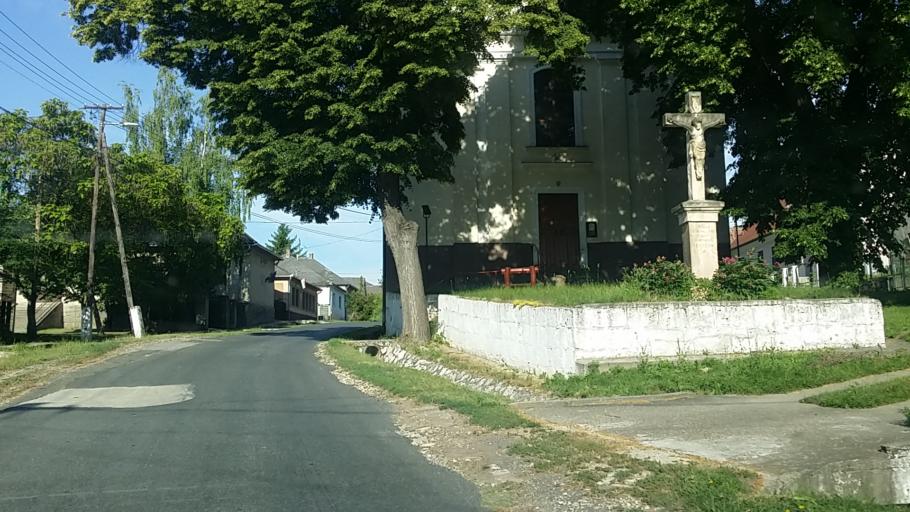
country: HU
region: Komarom-Esztergom
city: Sarisap
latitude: 47.6272
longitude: 18.7080
